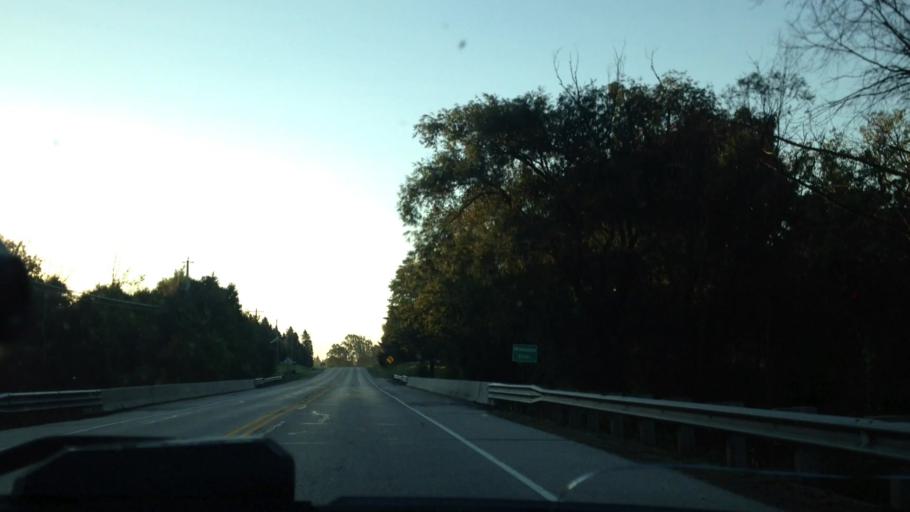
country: US
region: Wisconsin
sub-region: Washington County
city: Newburg
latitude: 43.4251
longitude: -88.0781
